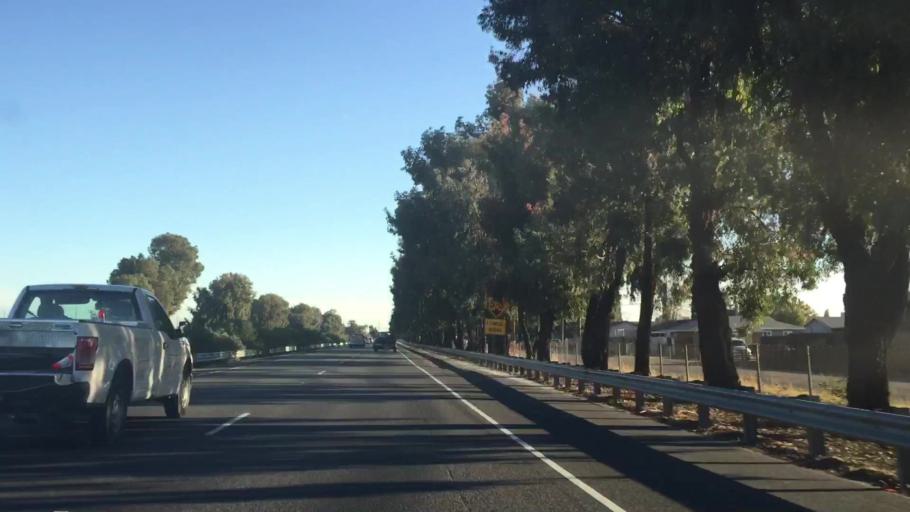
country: US
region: California
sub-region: Yuba County
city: Olivehurst
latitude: 39.1091
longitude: -121.5562
